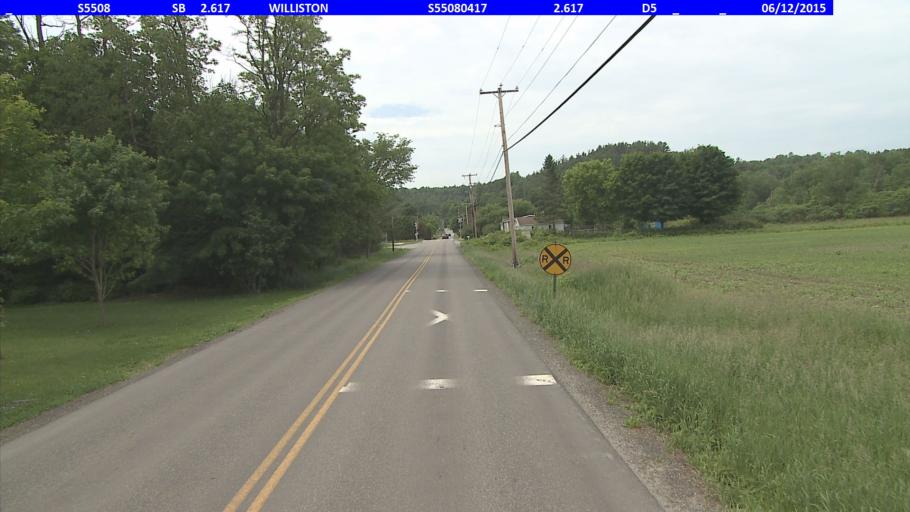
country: US
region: Vermont
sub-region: Chittenden County
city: Williston
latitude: 44.4681
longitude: -73.0457
